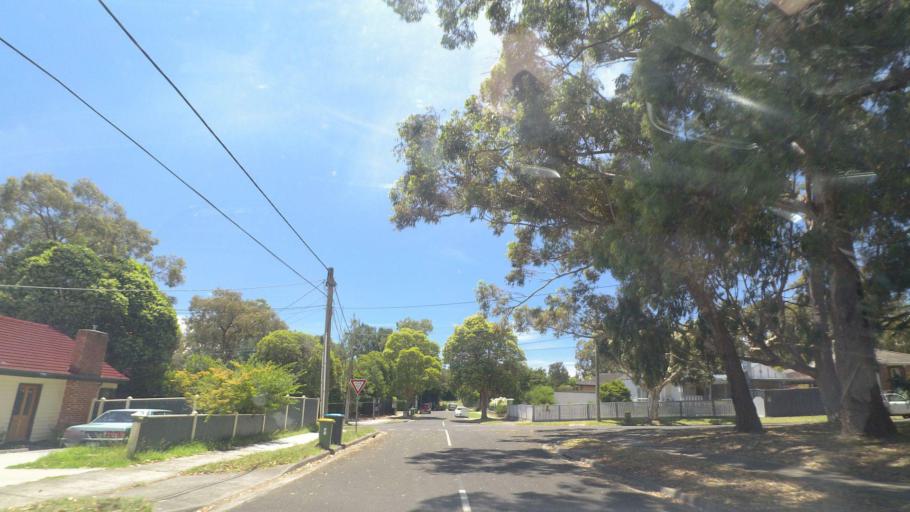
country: AU
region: Victoria
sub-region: Knox
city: Boronia
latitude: -37.8599
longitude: 145.2982
